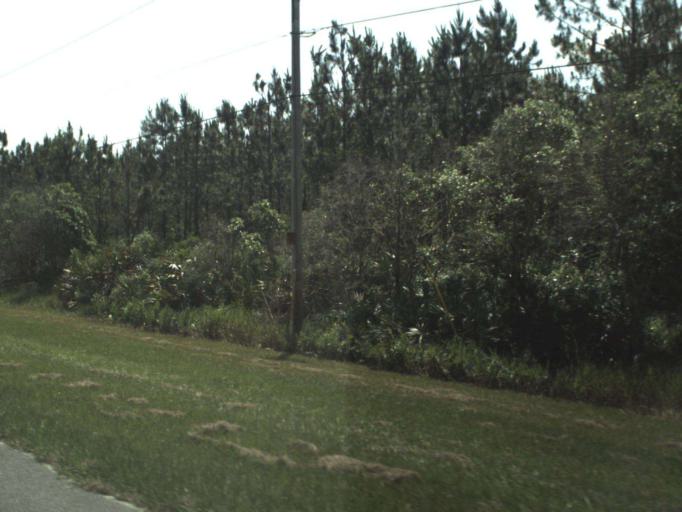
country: US
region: Florida
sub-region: Volusia County
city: Samsula-Spruce Creek
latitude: 29.1330
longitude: -81.1509
